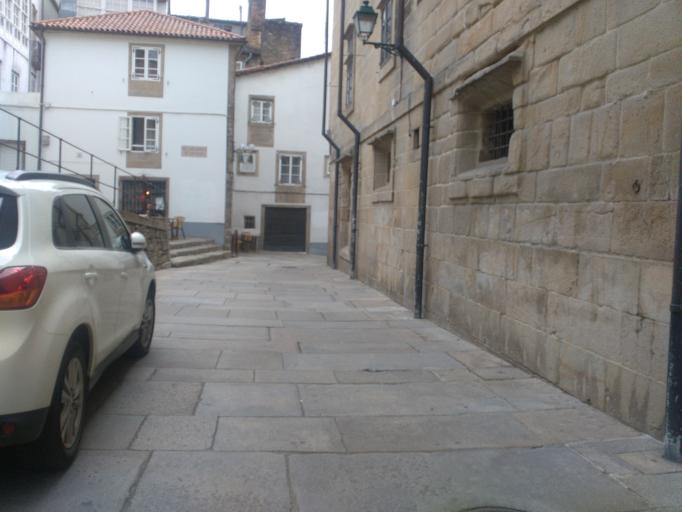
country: ES
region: Galicia
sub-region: Provincia da Coruna
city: Santiago de Compostela
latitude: 42.8817
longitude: -8.5438
